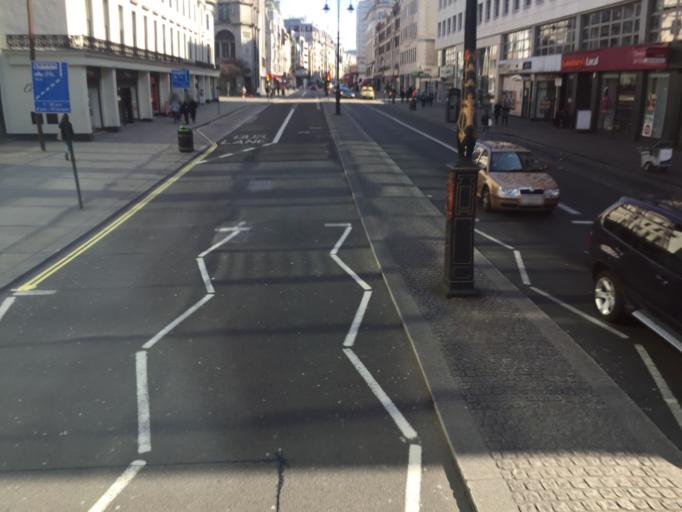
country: GB
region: England
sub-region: Greater London
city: London
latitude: 51.5088
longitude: -0.1250
